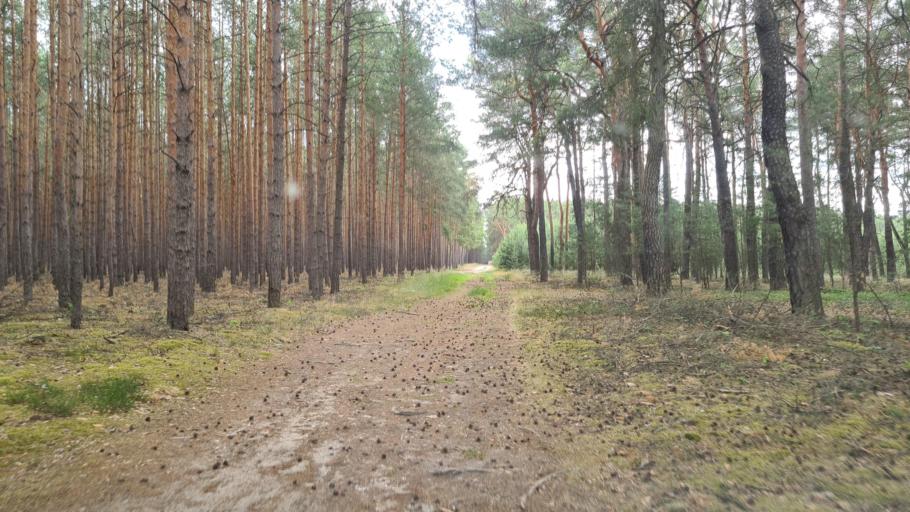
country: DE
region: Brandenburg
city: Crinitz
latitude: 51.6811
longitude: 13.7457
